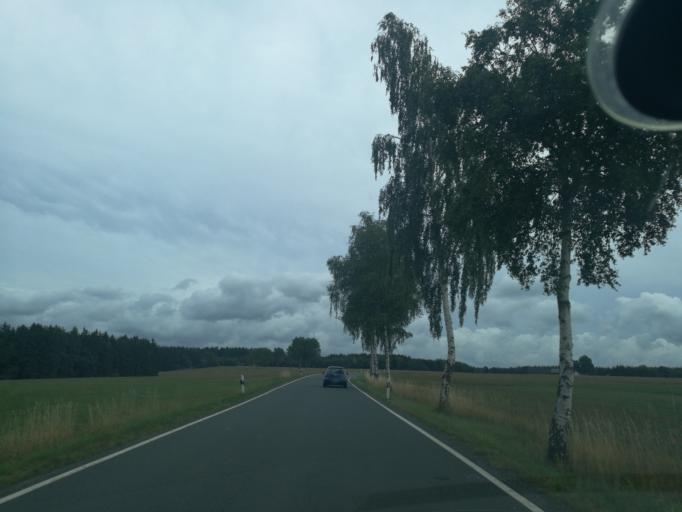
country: DE
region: Saxony
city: Eichigt
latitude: 50.3313
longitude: 12.1467
